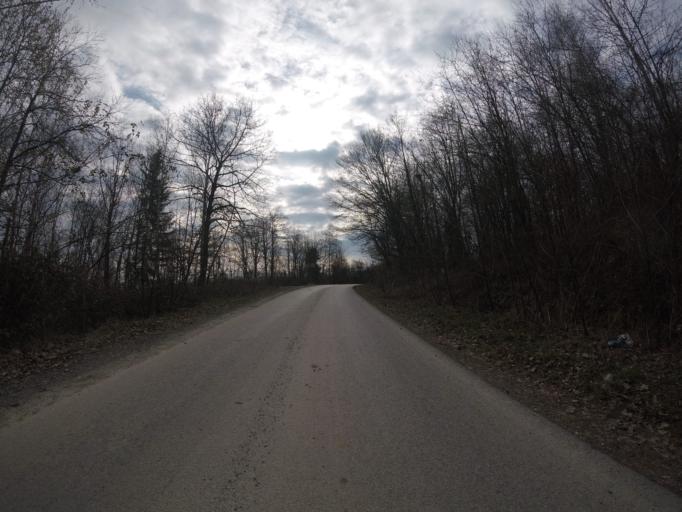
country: HR
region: Sisacko-Moslavacka
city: Glina
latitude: 45.4669
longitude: 16.0342
